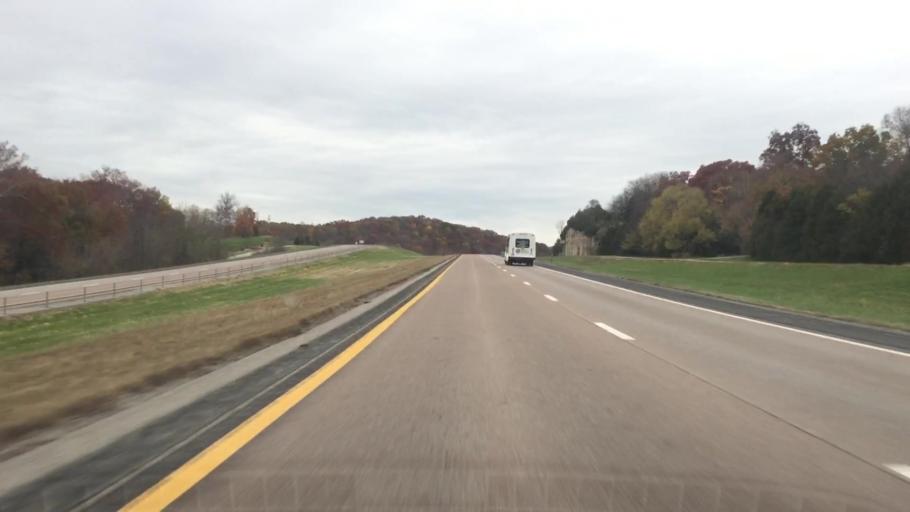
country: US
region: Missouri
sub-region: Cole County
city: Jefferson City
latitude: 38.6559
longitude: -92.2166
